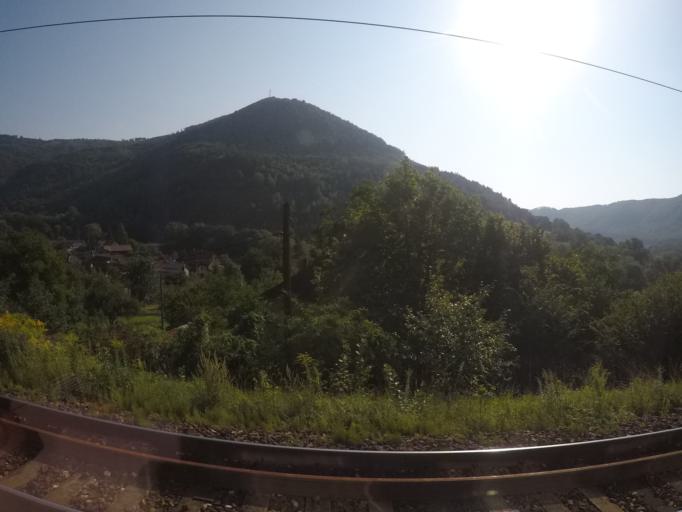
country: SK
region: Presovsky
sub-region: Okres Presov
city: Presov
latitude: 48.8571
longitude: 21.1550
